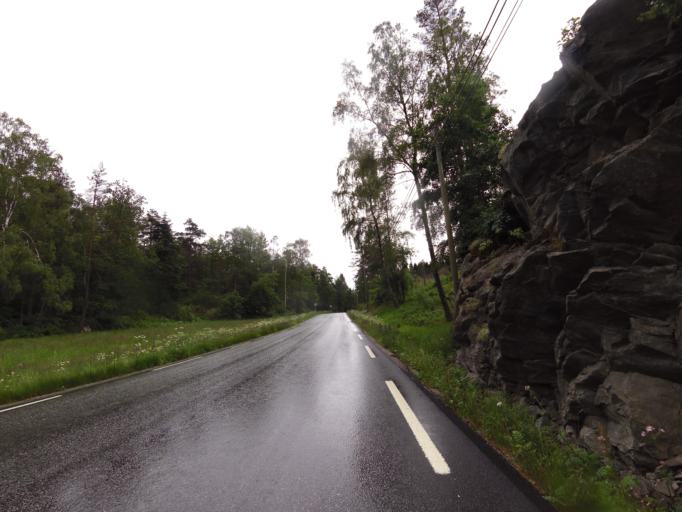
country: NO
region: Vest-Agder
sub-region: Mandal
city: Mandal
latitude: 58.0212
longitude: 7.5161
